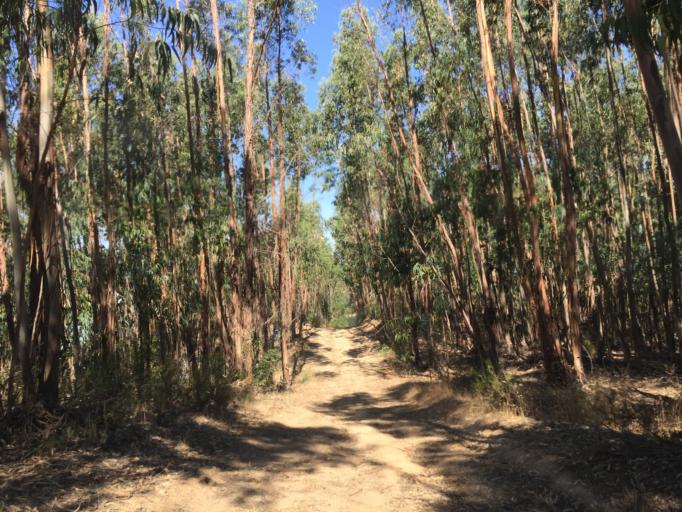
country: PT
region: Santarem
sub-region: Tomar
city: Tomar
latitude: 39.6129
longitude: -8.3551
